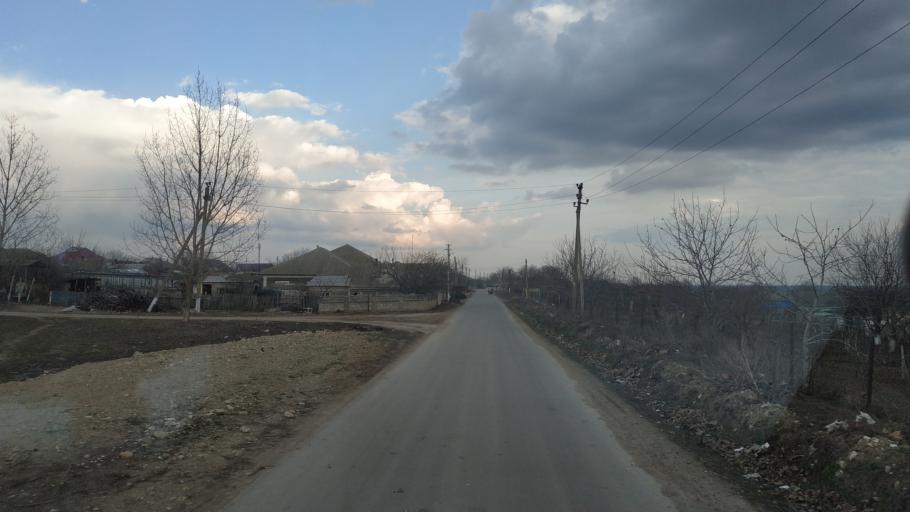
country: MD
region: Telenesti
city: Grigoriopol
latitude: 47.0097
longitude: 29.2968
